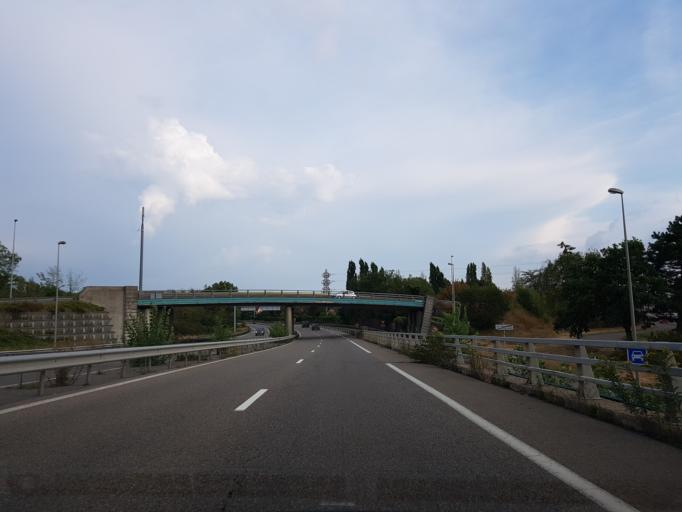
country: FR
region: Alsace
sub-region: Departement du Haut-Rhin
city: Kingersheim
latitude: 47.7884
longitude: 7.3162
